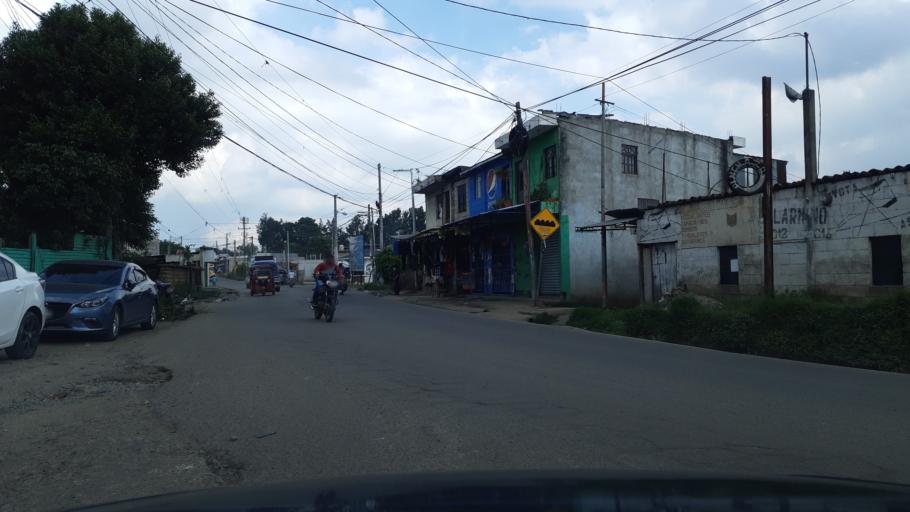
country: GT
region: Chimaltenango
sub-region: Municipio de Chimaltenango
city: Chimaltenango
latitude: 14.6717
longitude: -90.8067
